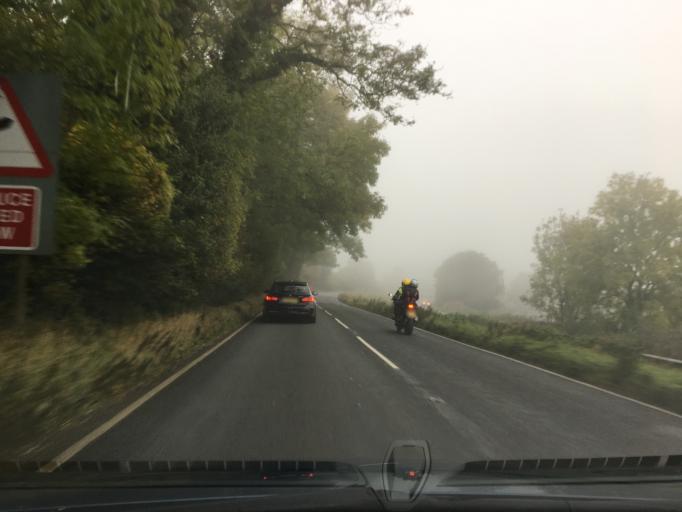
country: GB
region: England
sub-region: Hampshire
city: Four Marks
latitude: 51.1028
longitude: -1.0667
